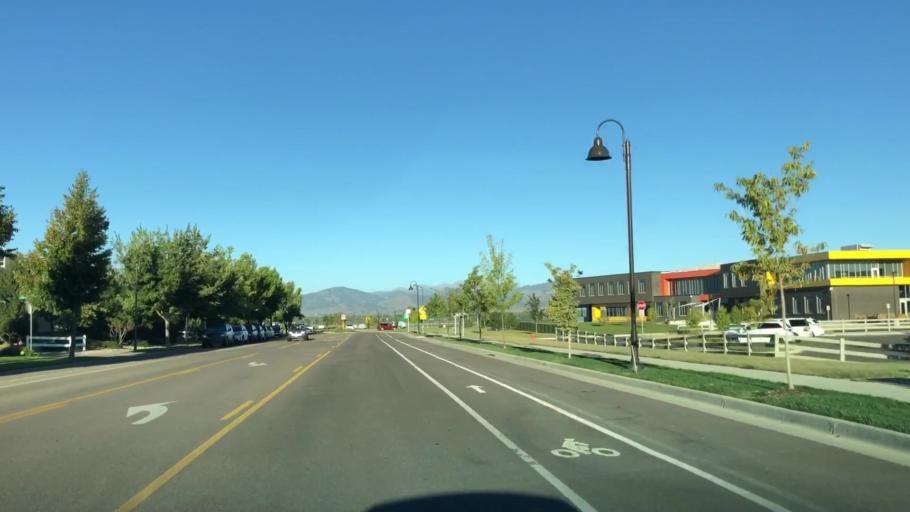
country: US
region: Colorado
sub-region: Larimer County
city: Loveland
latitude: 40.4145
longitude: -105.0183
